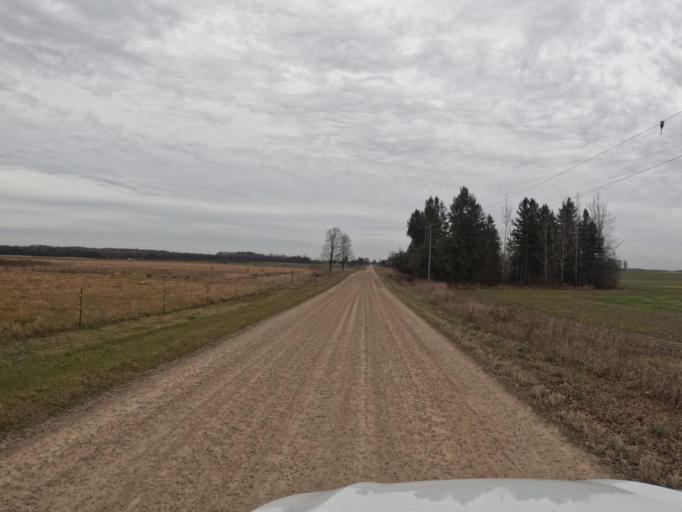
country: CA
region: Ontario
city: Shelburne
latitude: 44.0167
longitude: -80.3682
